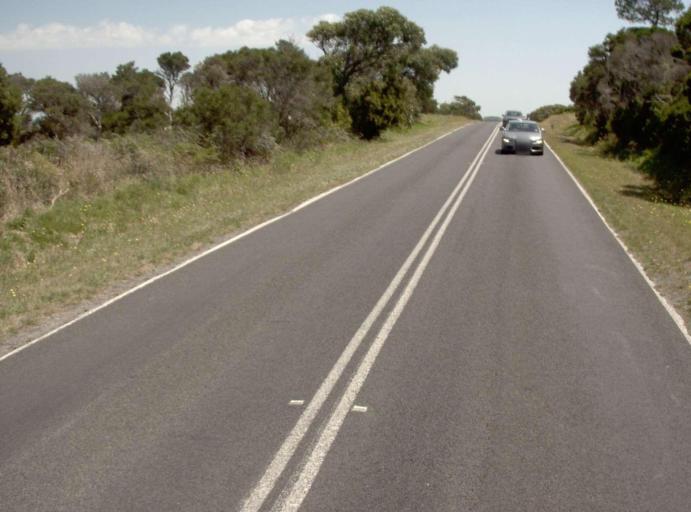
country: AU
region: Victoria
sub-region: Bass Coast
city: North Wonthaggi
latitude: -38.6500
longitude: 145.8539
